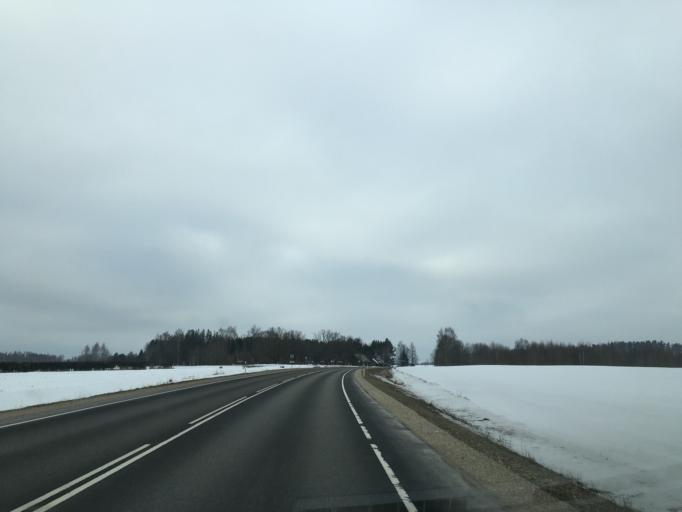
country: EE
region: Tartu
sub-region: Elva linn
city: Elva
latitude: 58.1901
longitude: 26.3504
